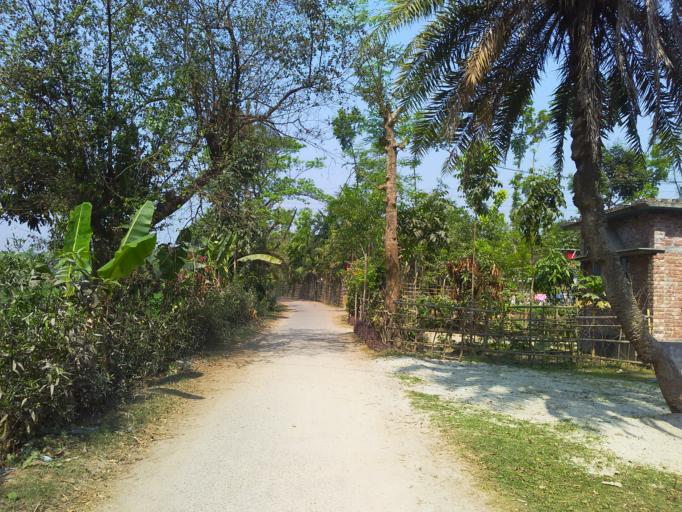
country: BD
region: Khulna
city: Khulna
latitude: 22.8809
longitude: 89.5409
